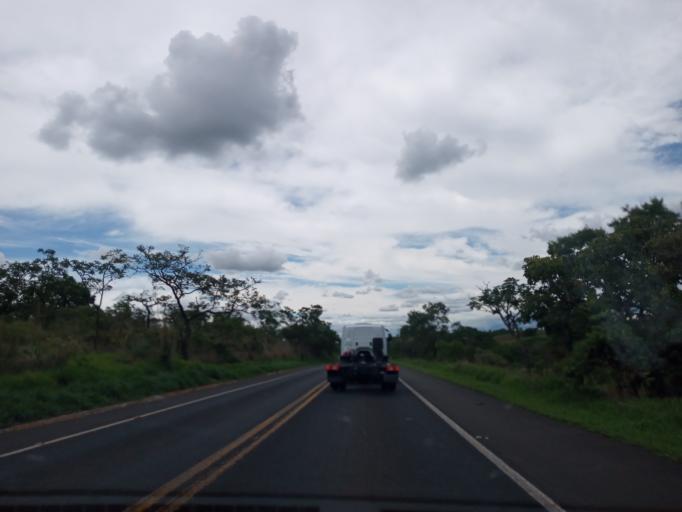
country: BR
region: Minas Gerais
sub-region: Uberlandia
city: Uberlandia
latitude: -19.1802
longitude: -47.8821
